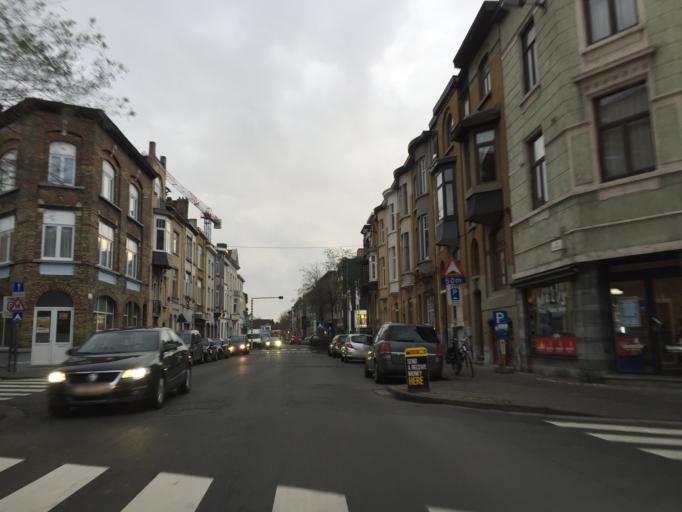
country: BE
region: Flanders
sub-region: Provincie Oost-Vlaanderen
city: Gent
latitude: 51.0641
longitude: 3.7261
